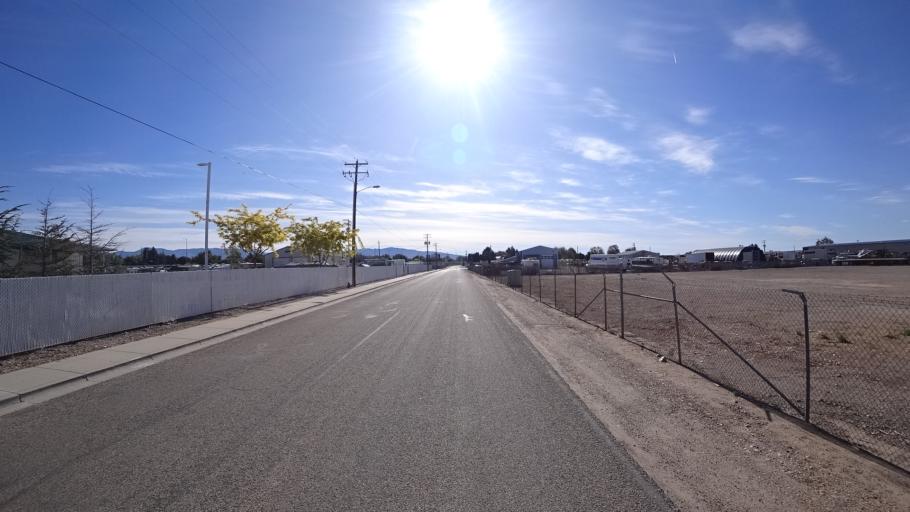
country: US
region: Idaho
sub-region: Ada County
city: Garden City
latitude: 43.5827
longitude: -116.2633
